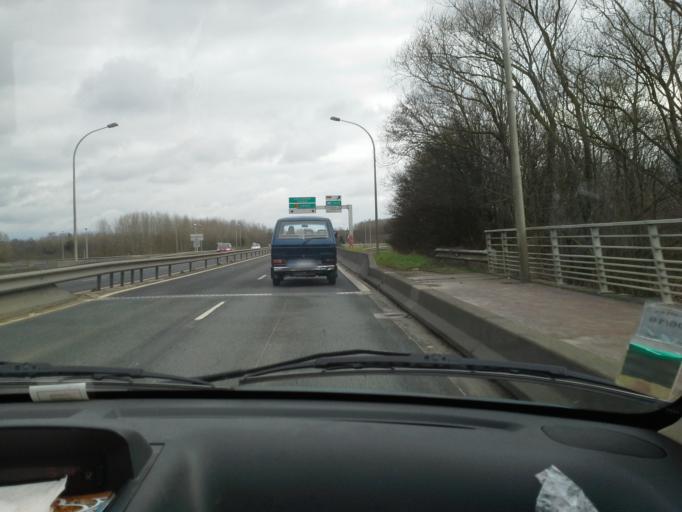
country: FR
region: Centre
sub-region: Departement du Loir-et-Cher
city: Vineuil
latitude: 47.5921
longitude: 1.3562
